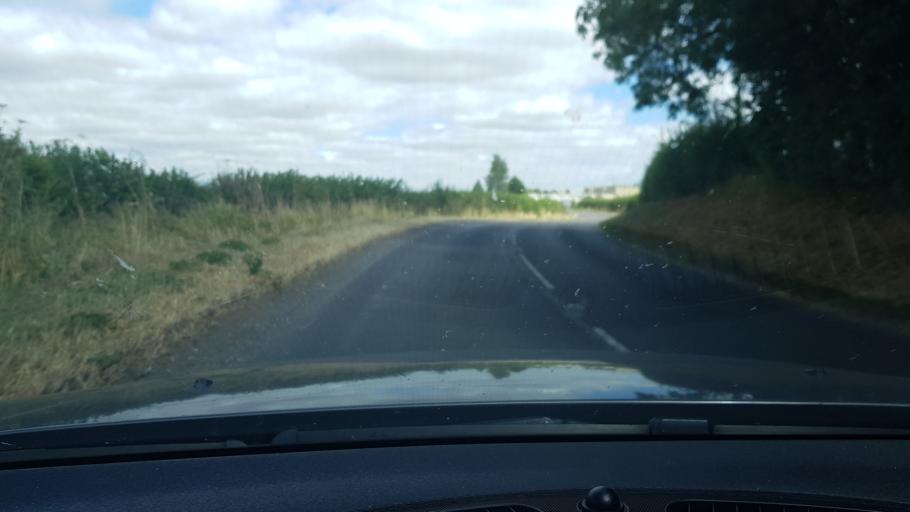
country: GB
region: England
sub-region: Wiltshire
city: Shalbourne
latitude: 51.3784
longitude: -1.5389
